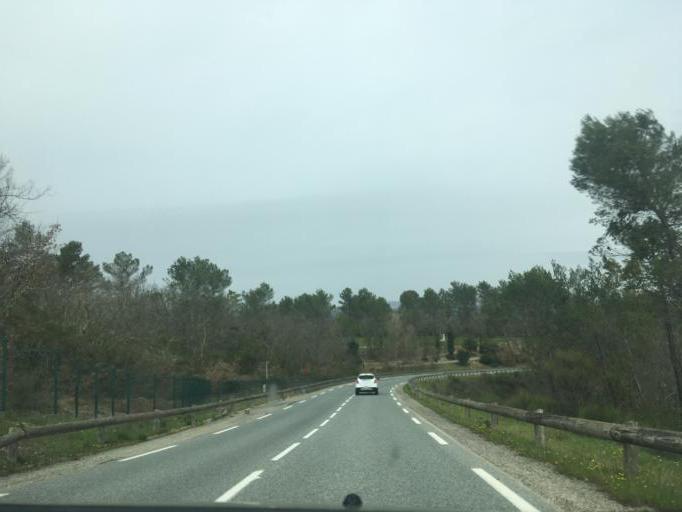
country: FR
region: Provence-Alpes-Cote d'Azur
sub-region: Departement du Var
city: Callian
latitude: 43.5933
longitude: 6.7418
